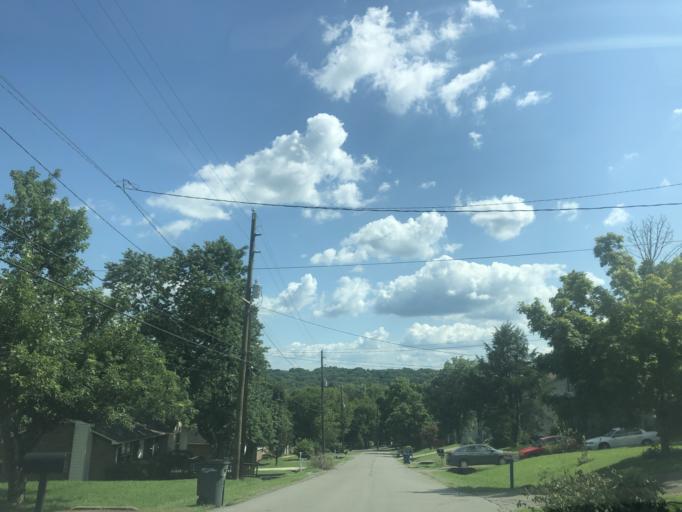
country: US
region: Tennessee
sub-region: Wilson County
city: Green Hill
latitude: 36.2082
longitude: -86.5872
